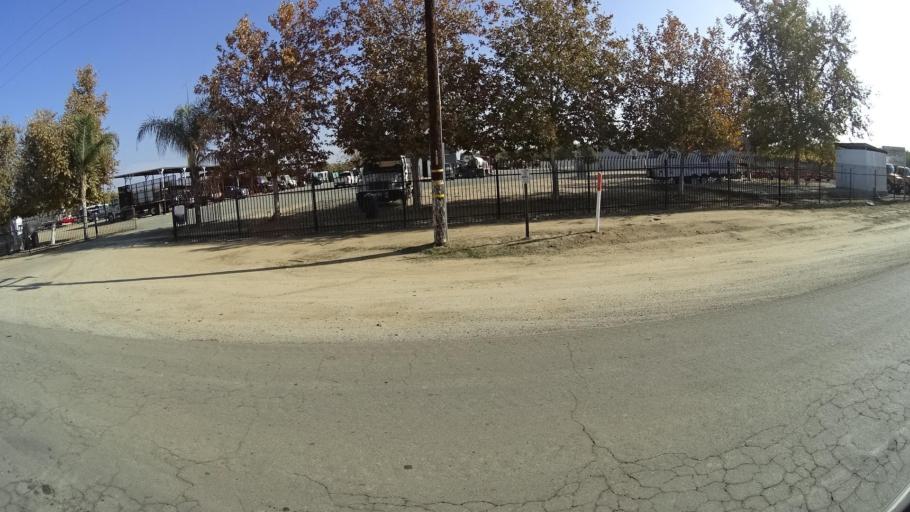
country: US
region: California
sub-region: Kern County
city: McFarland
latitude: 35.6700
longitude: -119.1693
